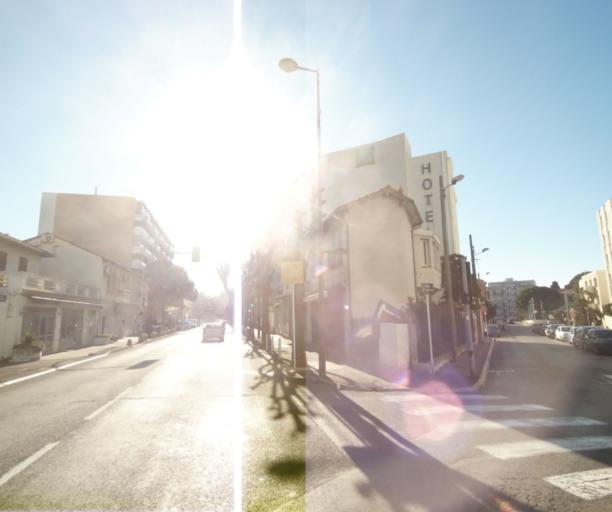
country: FR
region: Provence-Alpes-Cote d'Azur
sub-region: Departement des Alpes-Maritimes
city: Antibes
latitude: 43.5735
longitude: 7.1004
